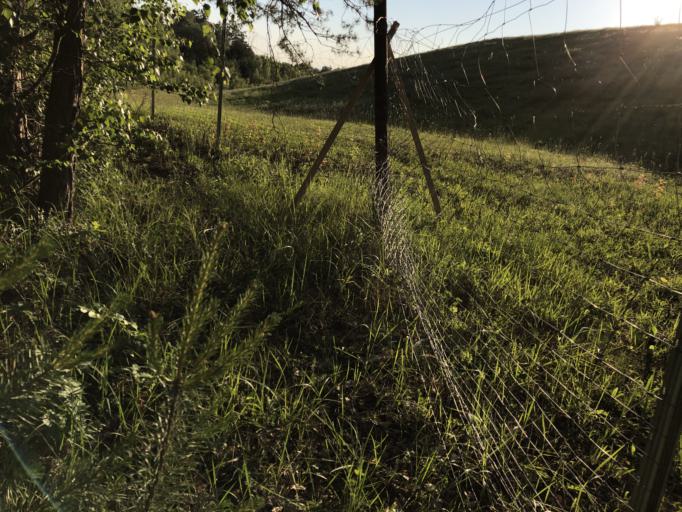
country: DE
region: Bavaria
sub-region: Upper Franconia
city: Memmelsdorf
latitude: 49.9139
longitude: 10.9503
